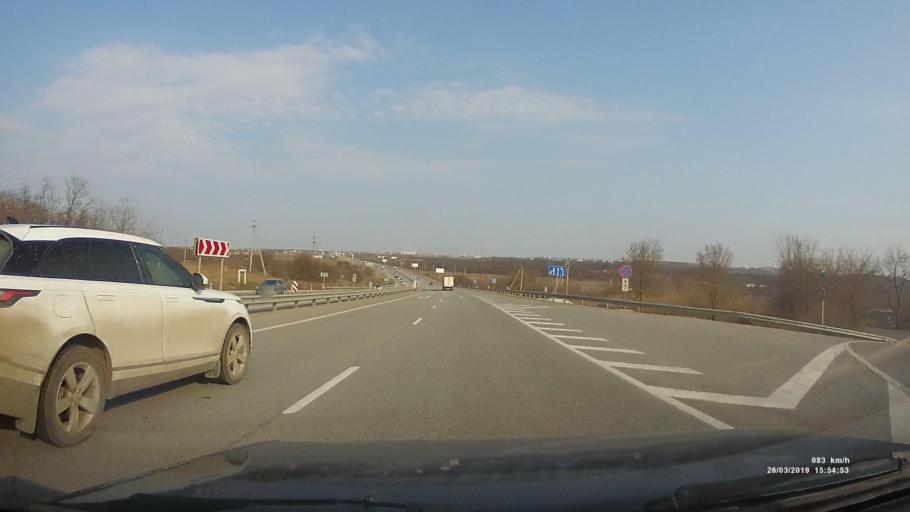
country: RU
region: Rostov
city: Kalinin
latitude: 47.2670
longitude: 39.5654
